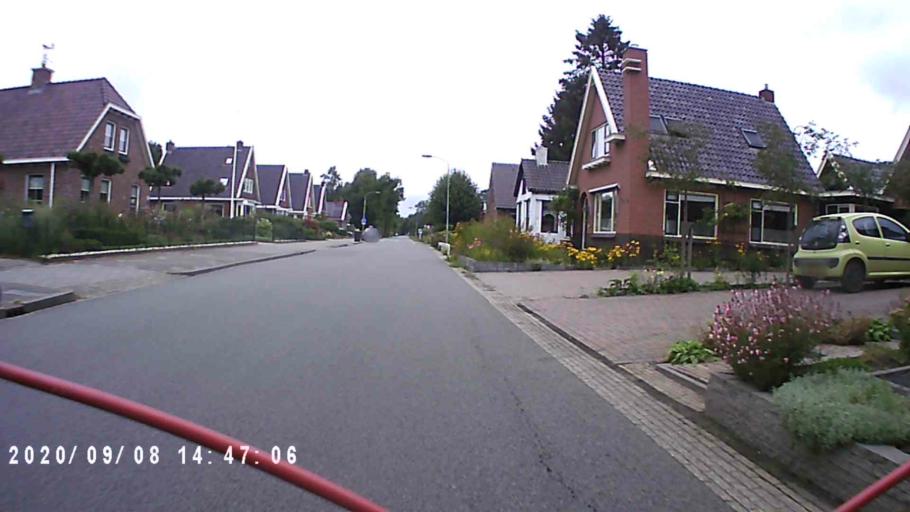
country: NL
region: Groningen
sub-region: Gemeente Slochteren
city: Slochteren
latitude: 53.2356
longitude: 6.8126
